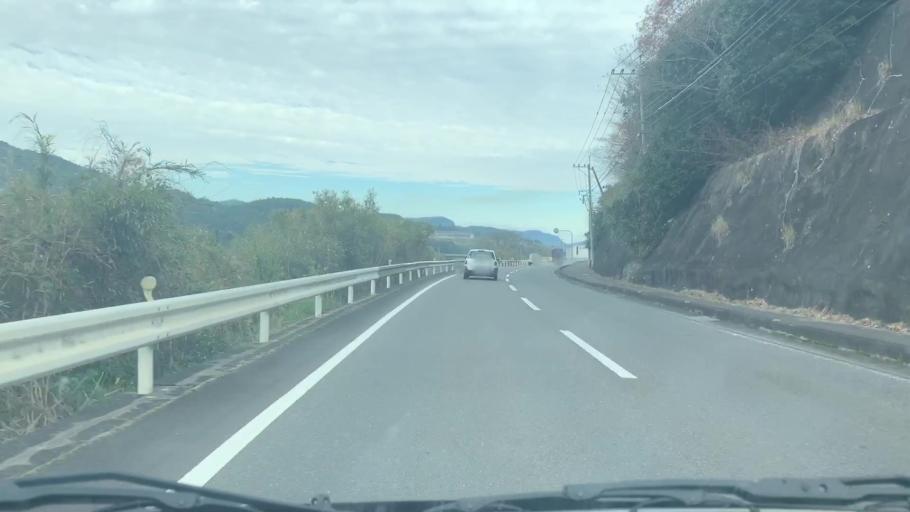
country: JP
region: Saga Prefecture
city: Imaricho-ko
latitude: 33.2760
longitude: 129.9650
